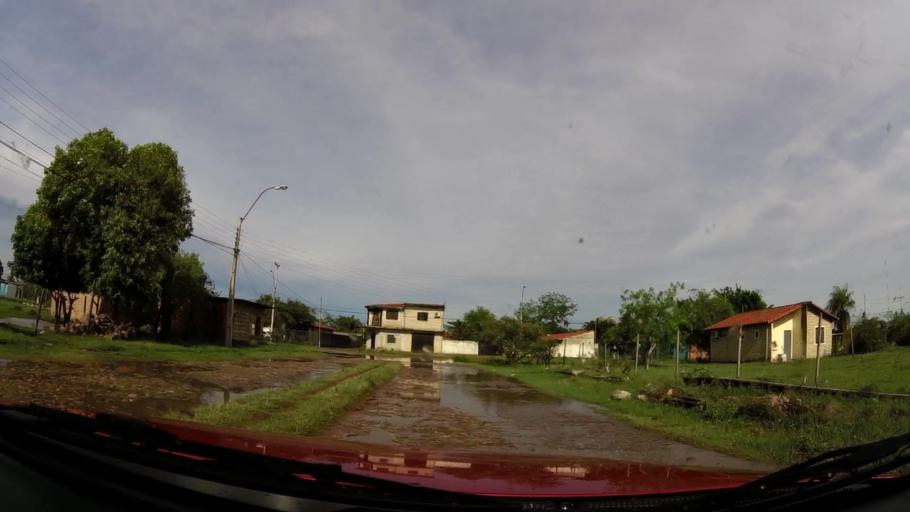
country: PY
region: Central
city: Limpio
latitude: -25.1676
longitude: -57.4893
